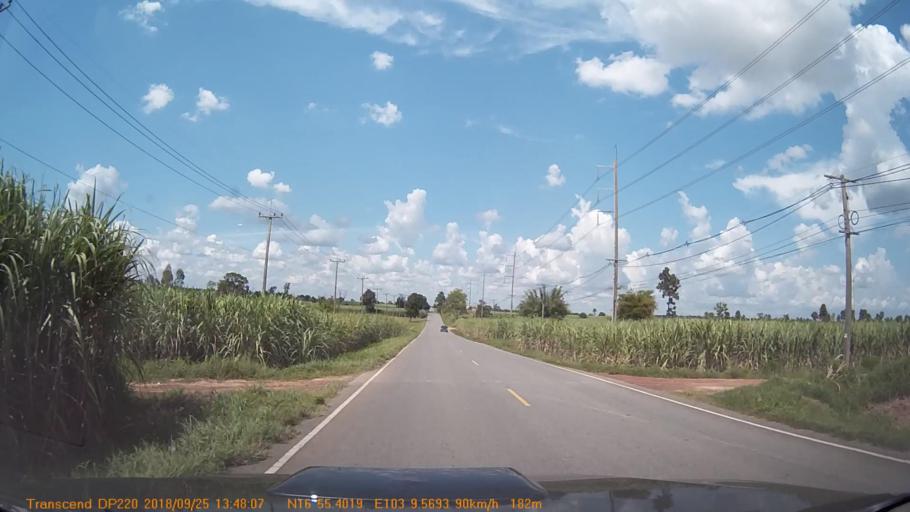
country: TH
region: Changwat Udon Thani
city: Si That
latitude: 16.9234
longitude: 103.1594
